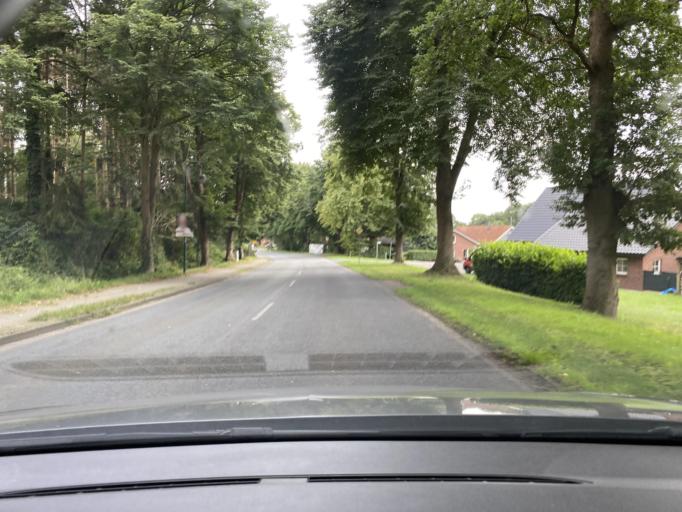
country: DE
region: Lower Saxony
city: Vollersode
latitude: 53.3216
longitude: 8.8996
